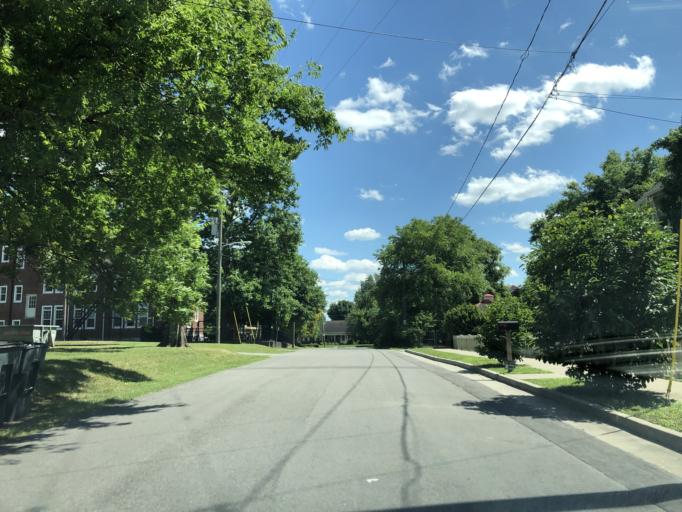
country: US
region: Tennessee
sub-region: Davidson County
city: Nashville
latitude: 36.1843
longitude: -86.7412
